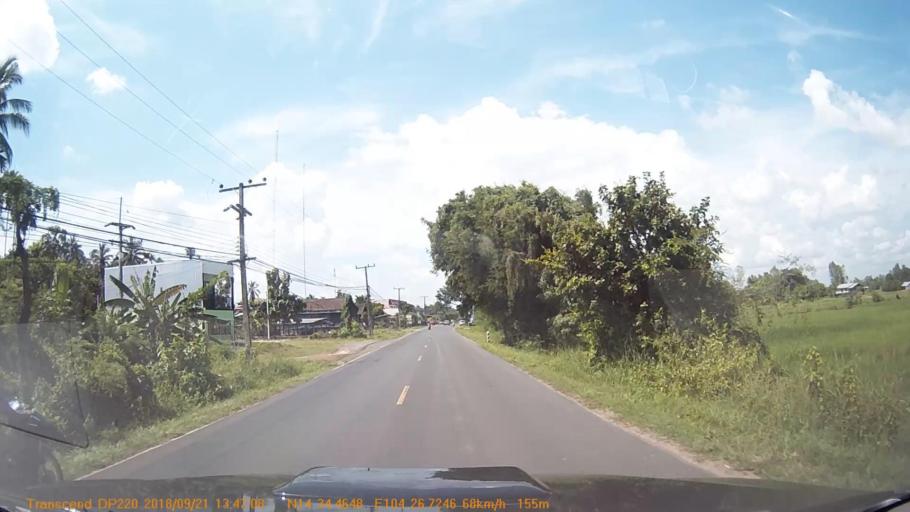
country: TH
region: Sisaket
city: Khun Han
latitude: 14.5747
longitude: 104.4453
